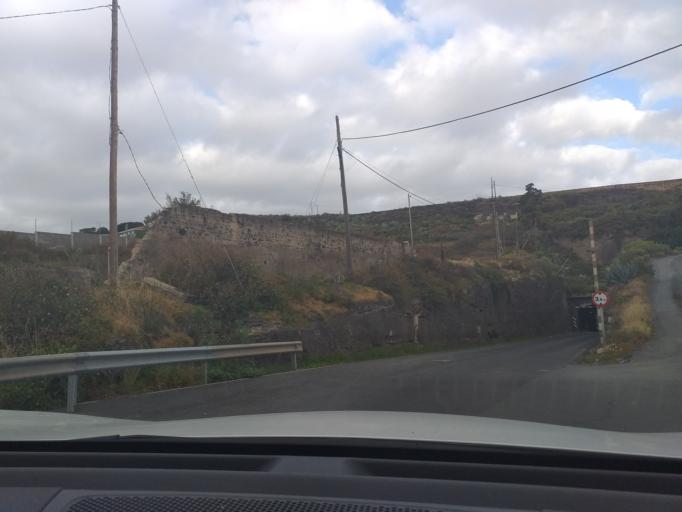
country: ES
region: Canary Islands
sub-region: Provincia de Las Palmas
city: Arucas
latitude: 28.1091
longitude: -15.4900
